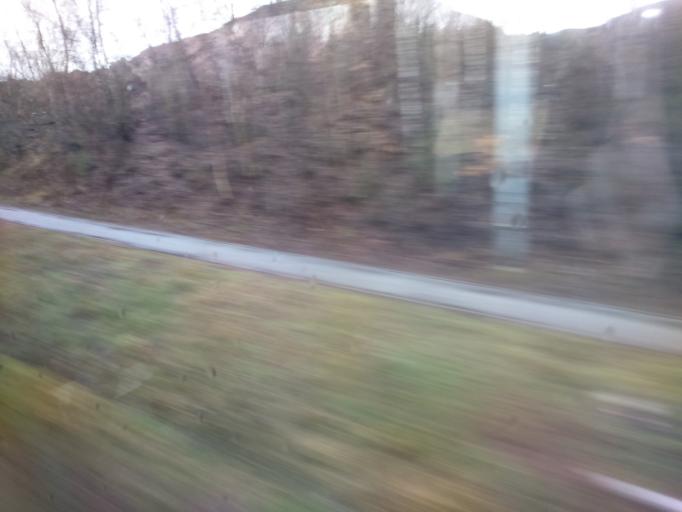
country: CZ
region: Plzensky
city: Zbuch
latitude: 49.6727
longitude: 13.2173
